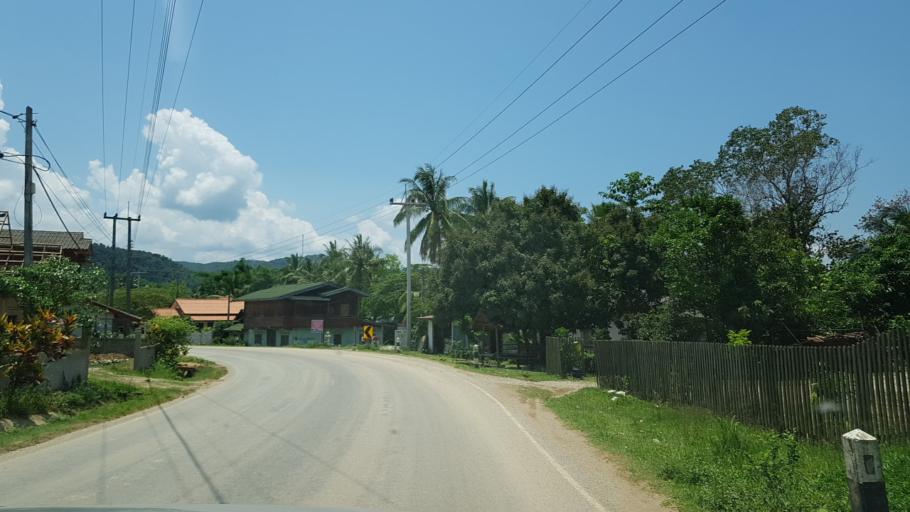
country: LA
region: Vientiane
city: Muang Kasi
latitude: 19.2400
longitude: 102.2503
